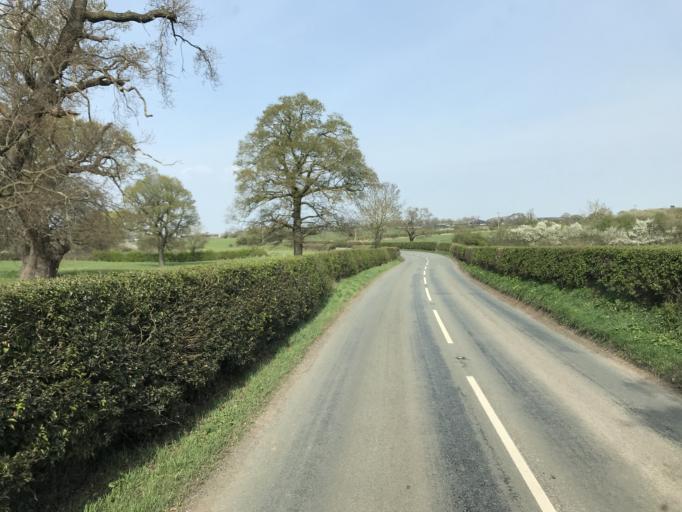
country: GB
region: England
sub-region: Cheshire West and Chester
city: Eccleston
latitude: 53.1501
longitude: -2.8620
